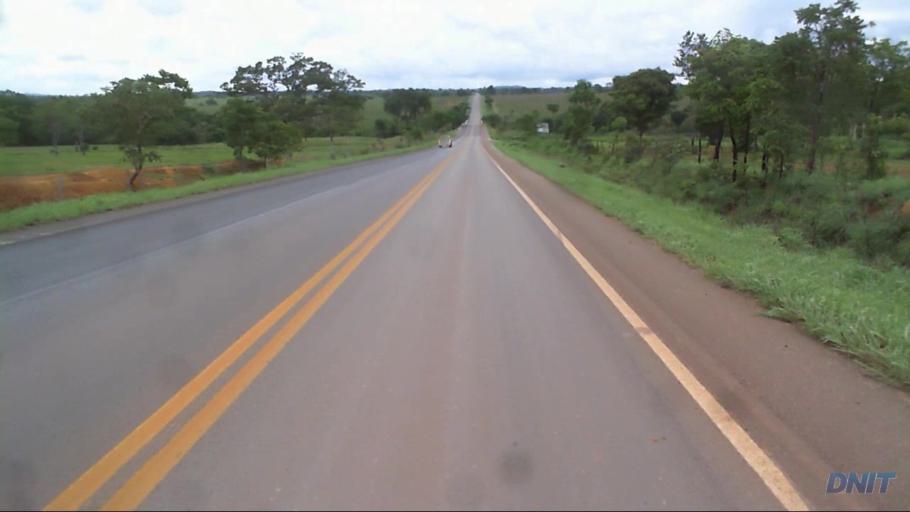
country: BR
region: Goias
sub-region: Padre Bernardo
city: Padre Bernardo
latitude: -15.1560
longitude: -48.3236
